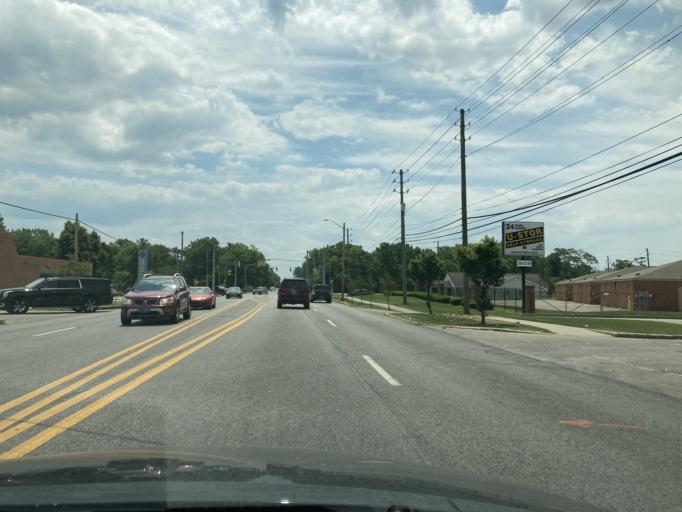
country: US
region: Indiana
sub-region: Marion County
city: Meridian Hills
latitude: 39.8801
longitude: -86.2076
